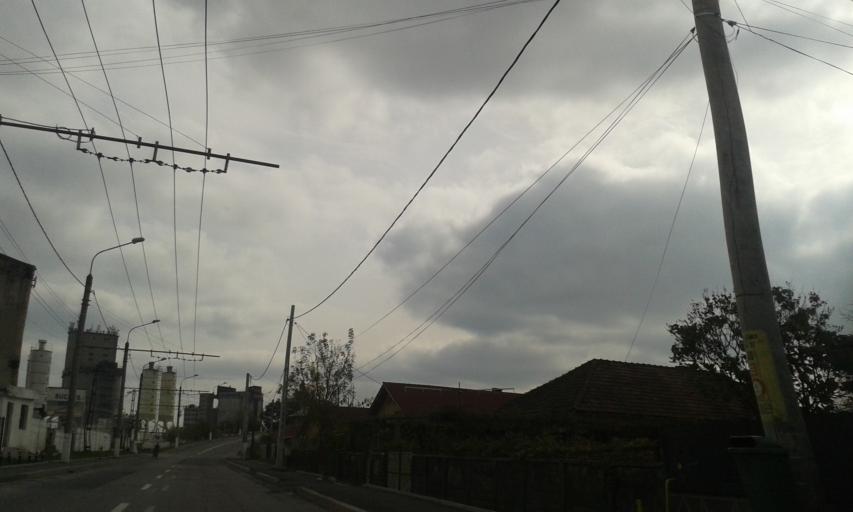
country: RO
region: Gorj
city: Targu Jiu
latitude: 45.0746
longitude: 23.3021
